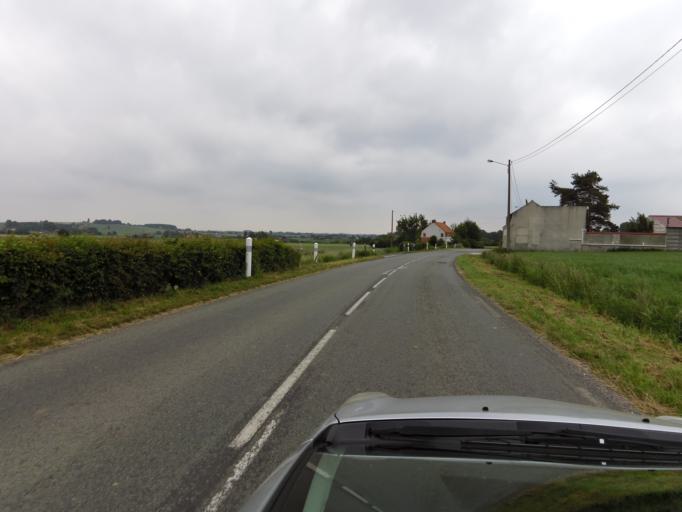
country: FR
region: Nord-Pas-de-Calais
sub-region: Departement du Nord
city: Bailleul
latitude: 50.7545
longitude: 2.7493
